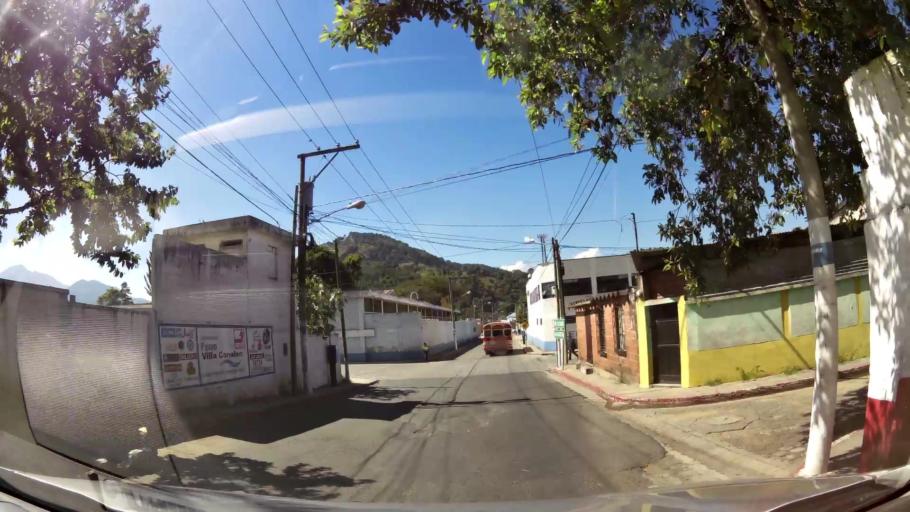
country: GT
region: Guatemala
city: Villa Canales
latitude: 14.4818
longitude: -90.5326
